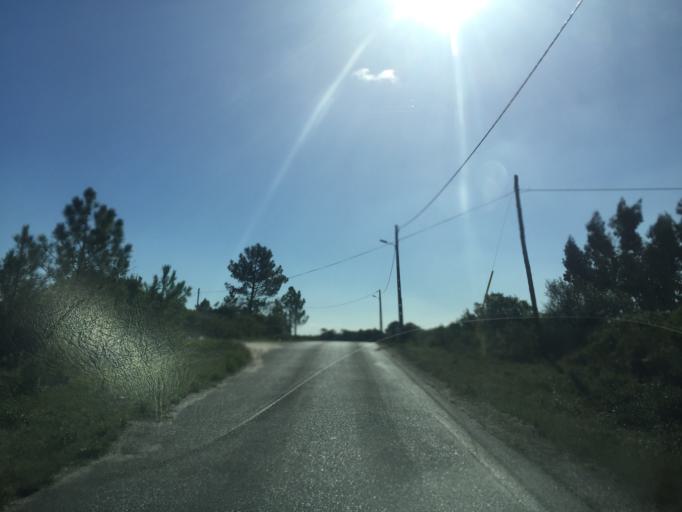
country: PT
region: Coimbra
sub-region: Figueira da Foz
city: Tavarede
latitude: 40.1936
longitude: -8.8435
